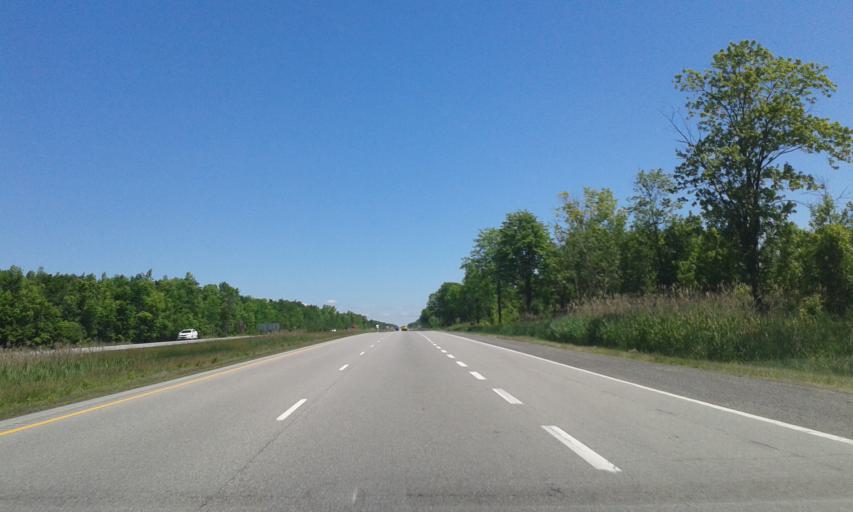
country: US
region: New York
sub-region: St. Lawrence County
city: Ogdensburg
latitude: 44.8106
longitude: -75.4050
